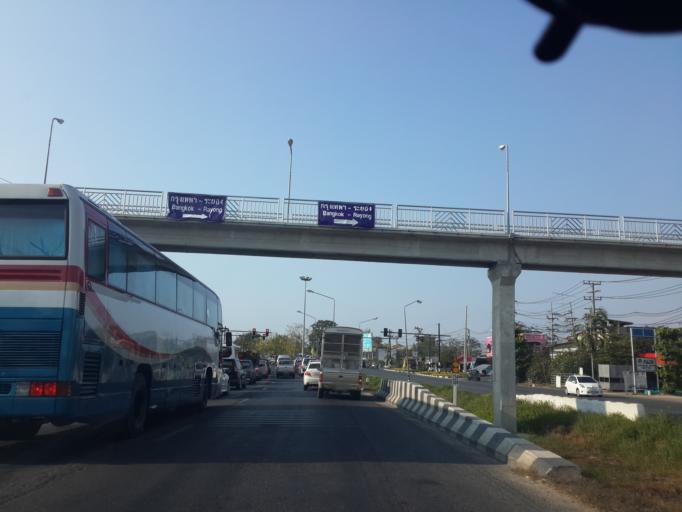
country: TH
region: Chon Buri
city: Phatthaya
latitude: 12.8563
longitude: 100.9090
